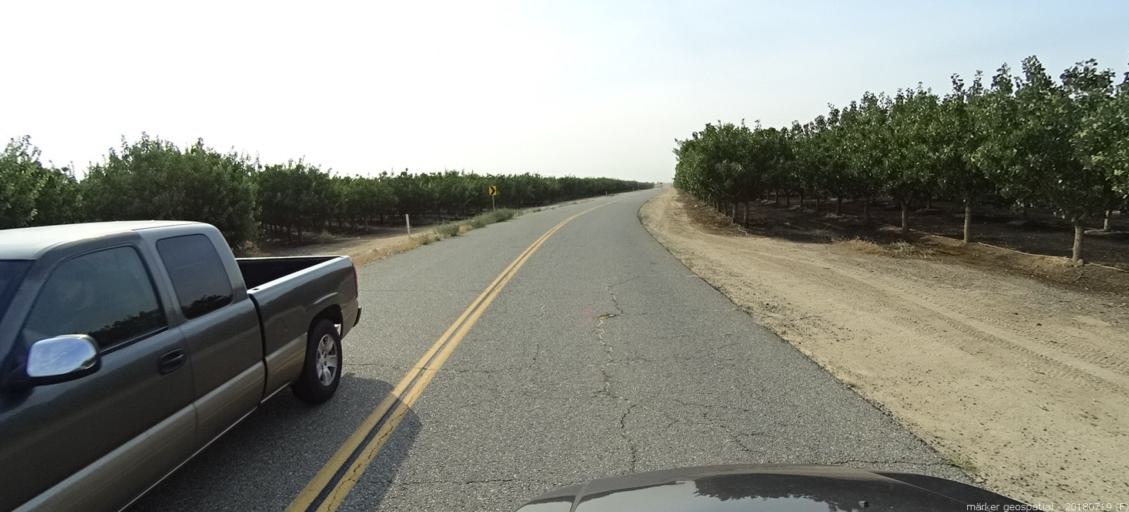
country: US
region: California
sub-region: Madera County
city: Fairmead
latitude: 37.0496
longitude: -120.1626
